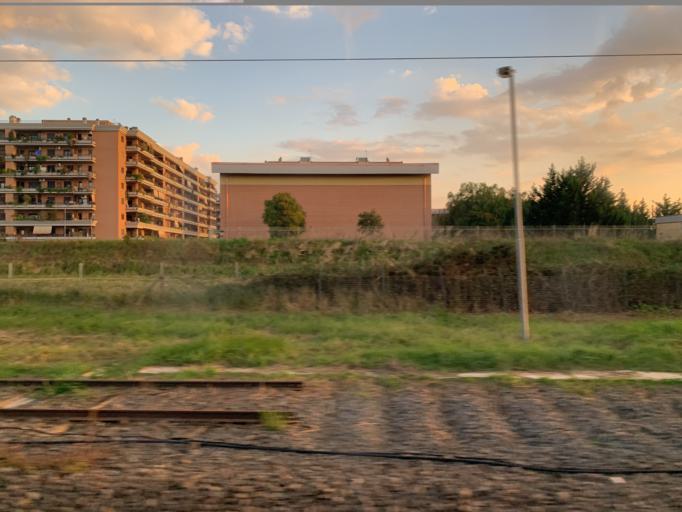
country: IT
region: Latium
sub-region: Citta metropolitana di Roma Capitale
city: Npp 23 (Parco Leonardo)
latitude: 41.8039
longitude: 12.3047
